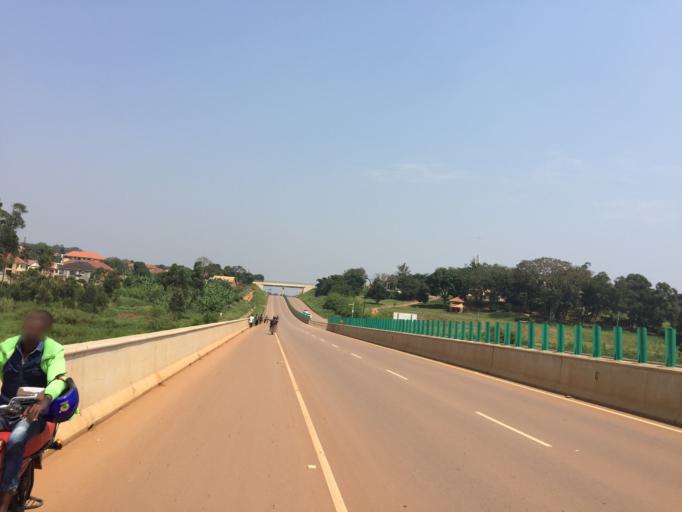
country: UG
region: Central Region
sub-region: Kampala District
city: Kampala
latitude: 0.2375
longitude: 32.6139
